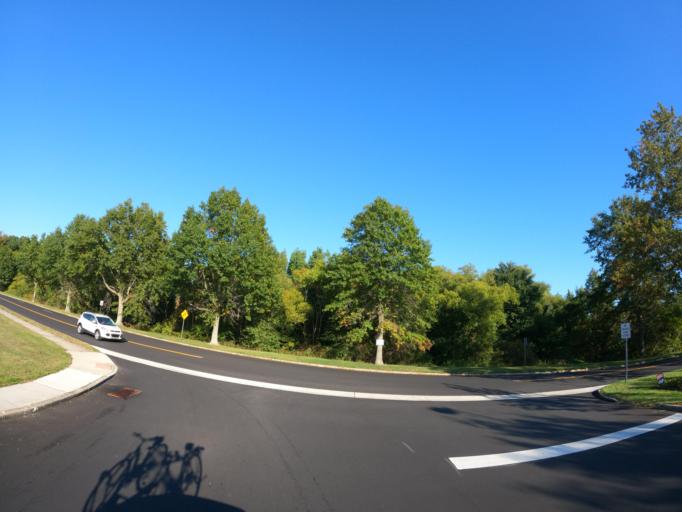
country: US
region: New Jersey
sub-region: Cape May County
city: North Cape May
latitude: 38.9752
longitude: -74.9360
